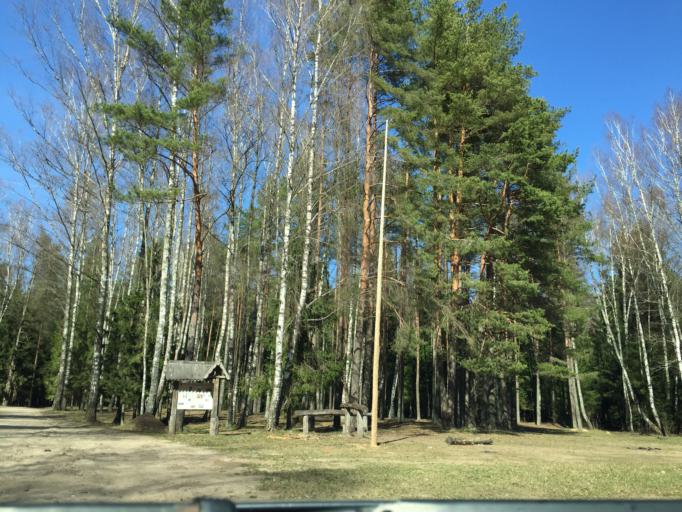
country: LT
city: Kursenai
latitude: 55.8301
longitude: 22.9934
